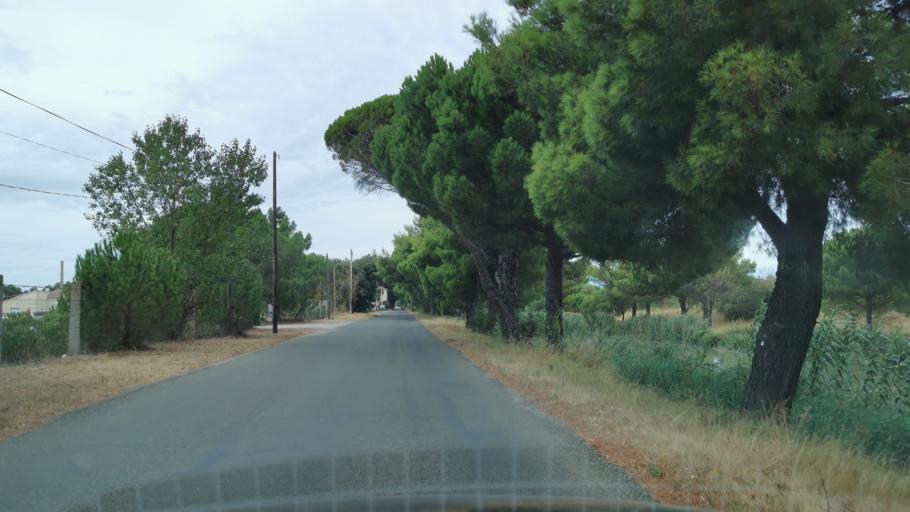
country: FR
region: Languedoc-Roussillon
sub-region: Departement de l'Aude
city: Saint-Marcel-sur-Aude
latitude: 43.2703
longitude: 2.9359
